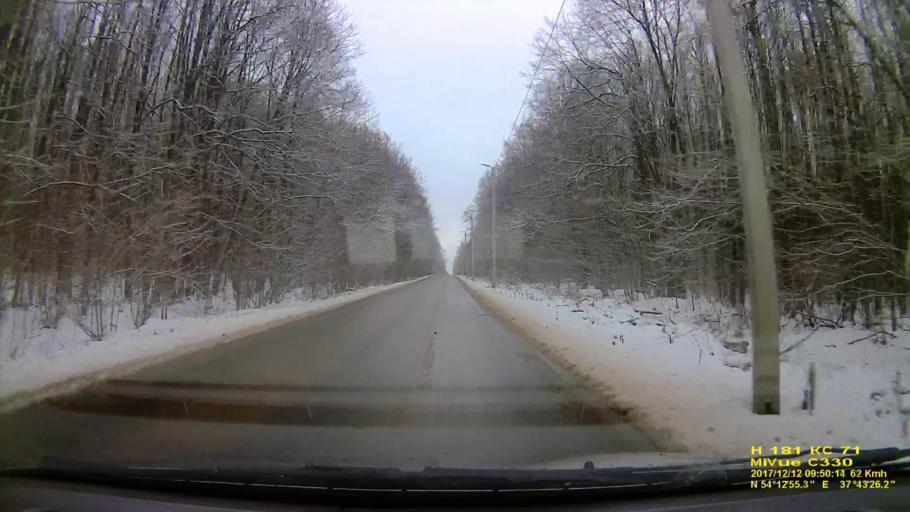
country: RU
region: Tula
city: Tula
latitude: 54.2154
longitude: 37.7246
